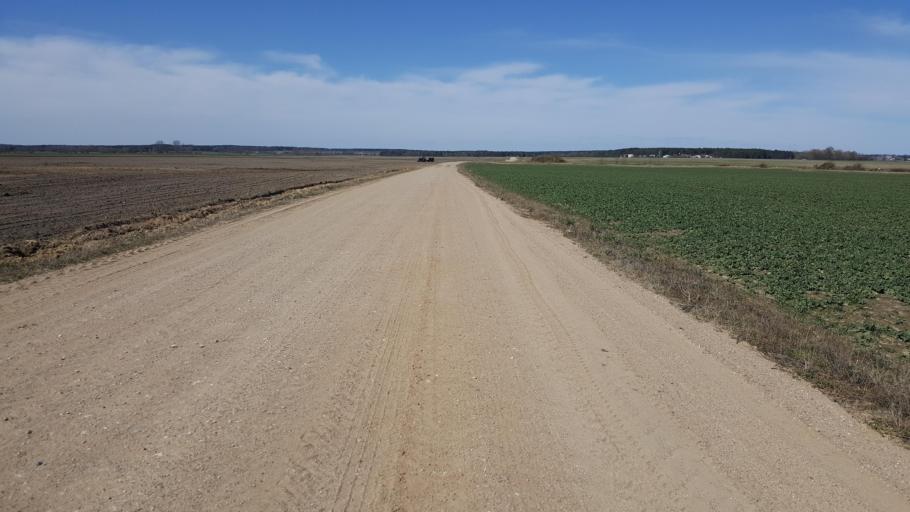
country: BY
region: Brest
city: Kamyanyets
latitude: 52.3001
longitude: 23.9085
